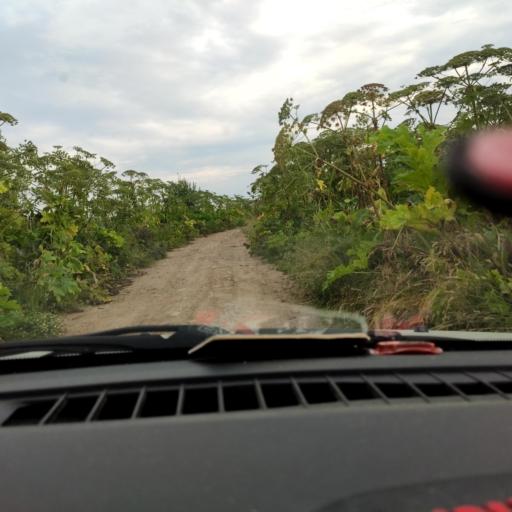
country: RU
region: Perm
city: Kultayevo
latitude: 57.8564
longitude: 55.9734
